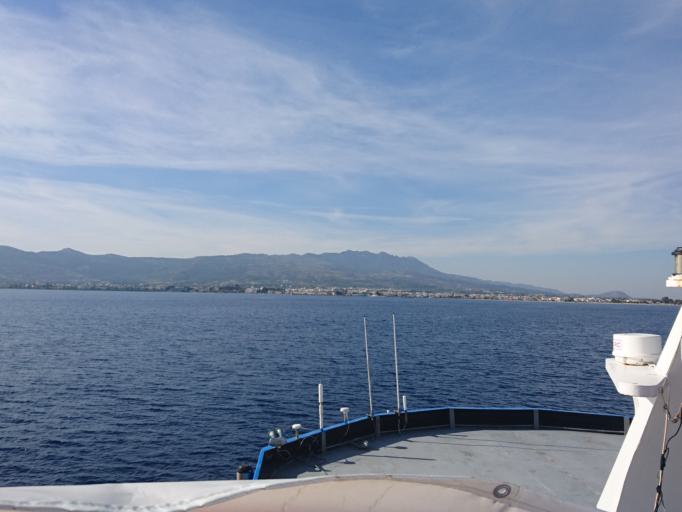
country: GR
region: South Aegean
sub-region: Nomos Dodekanisou
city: Kos
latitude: 36.9108
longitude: 27.3028
